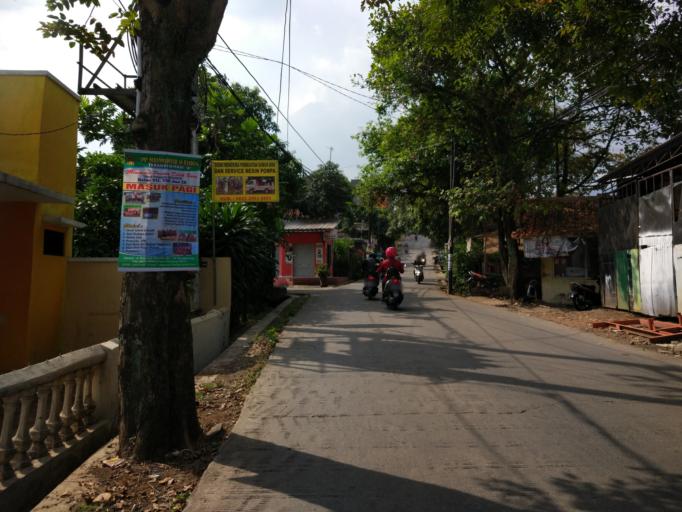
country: ID
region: West Java
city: Cileunyi
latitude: -6.9046
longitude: 107.6907
